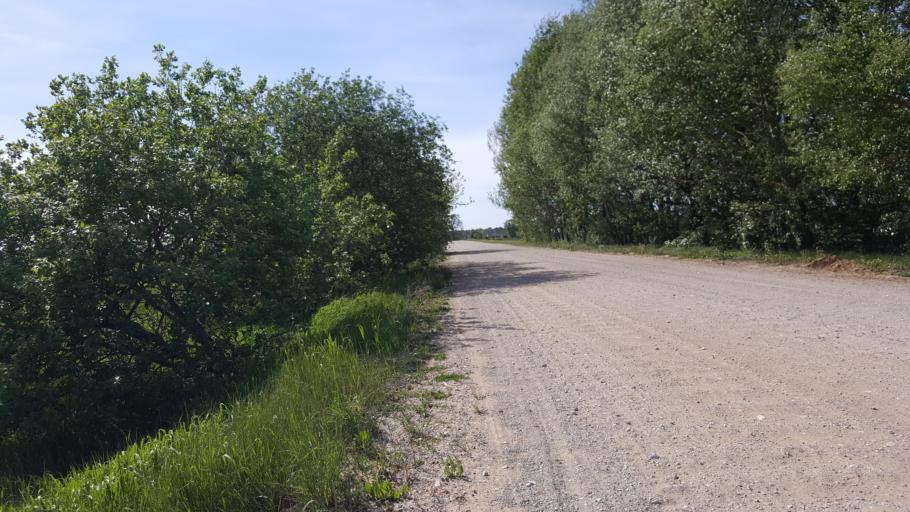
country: BY
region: Brest
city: Zhabinka
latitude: 52.3143
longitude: 24.0469
